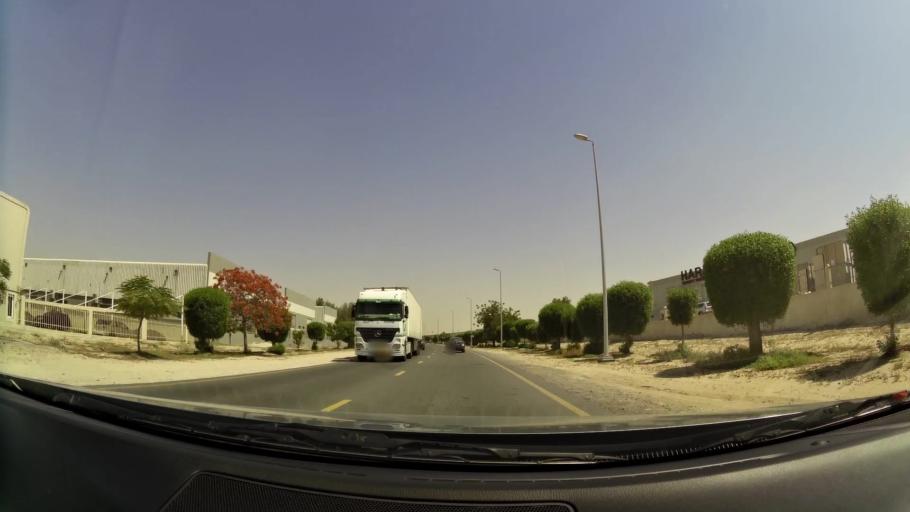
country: AE
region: Dubai
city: Dubai
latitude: 24.9871
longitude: 55.1556
